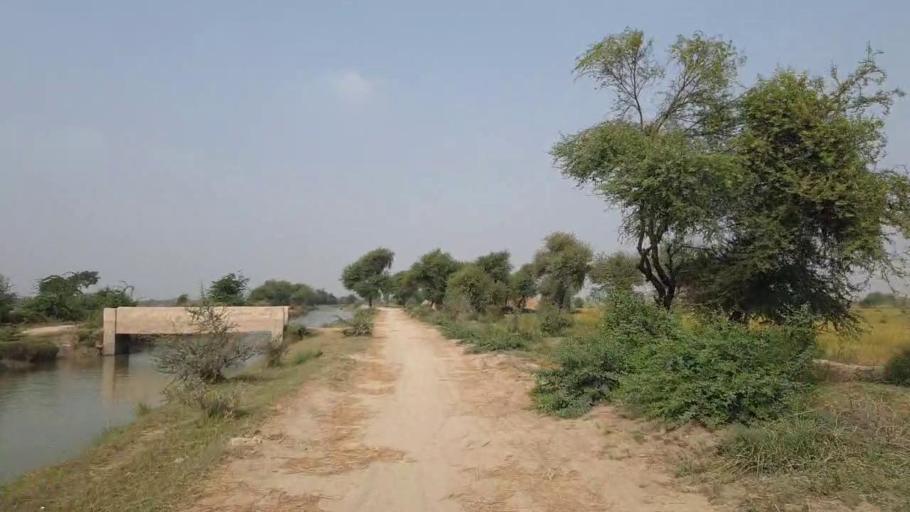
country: PK
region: Sindh
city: Kario
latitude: 24.8400
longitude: 68.5395
